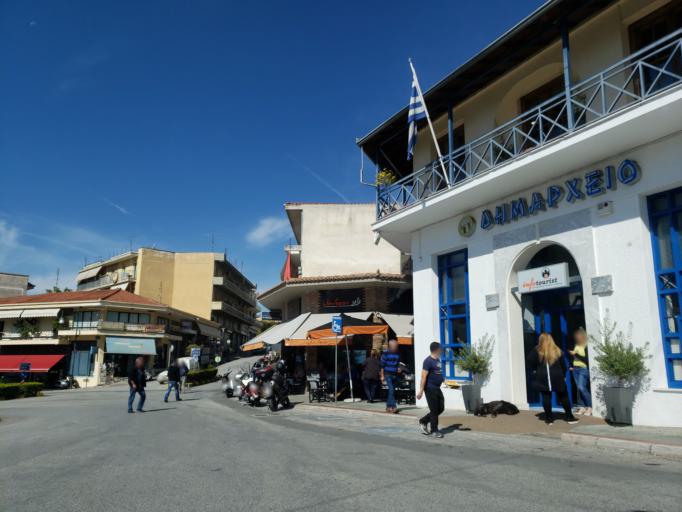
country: GR
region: Thessaly
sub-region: Trikala
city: Kalampaka
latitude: 39.7070
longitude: 21.6232
